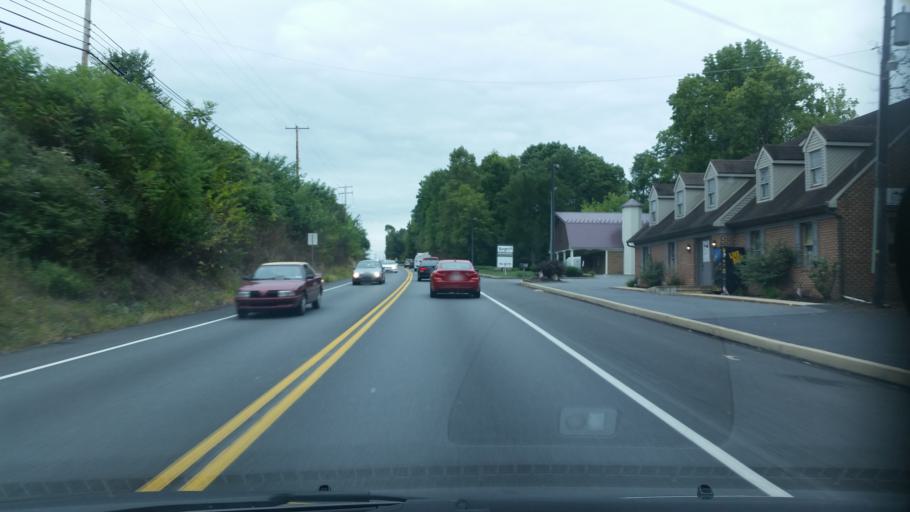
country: US
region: Pennsylvania
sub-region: Lancaster County
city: Willow Street
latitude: 39.9970
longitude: -76.2896
